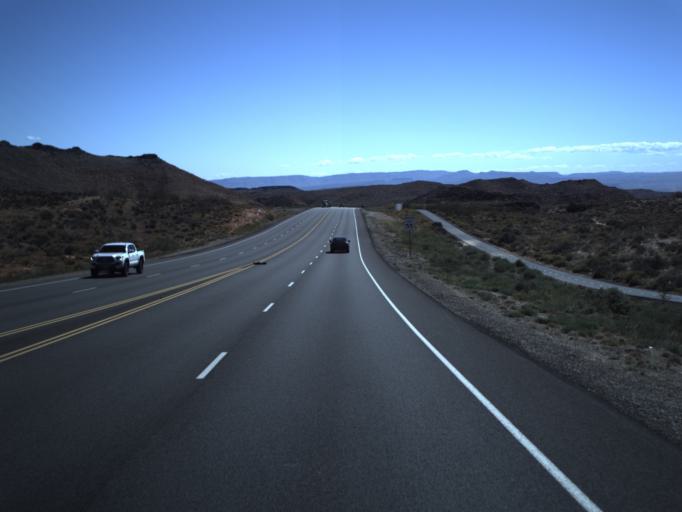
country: US
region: Utah
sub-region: Washington County
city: Santa Clara
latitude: 37.1677
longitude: -113.6155
